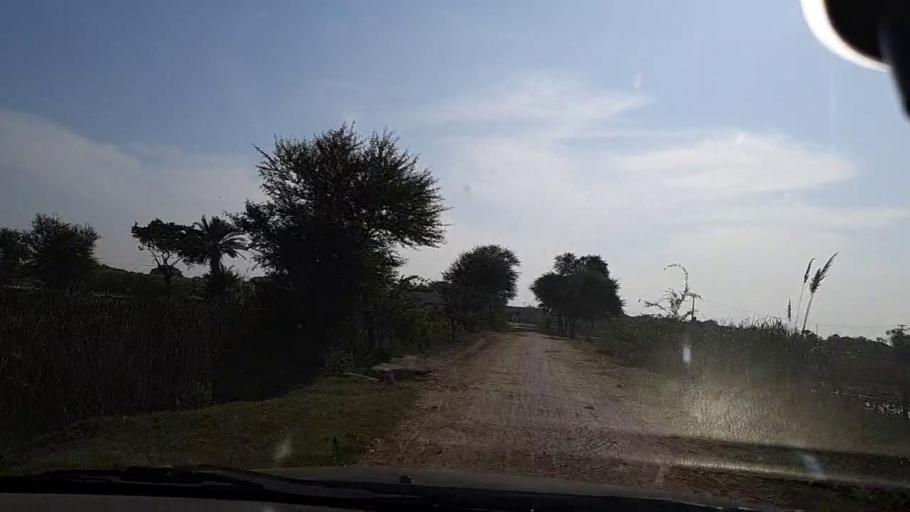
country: PK
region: Sindh
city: Mirpur Batoro
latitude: 24.6154
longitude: 68.2697
